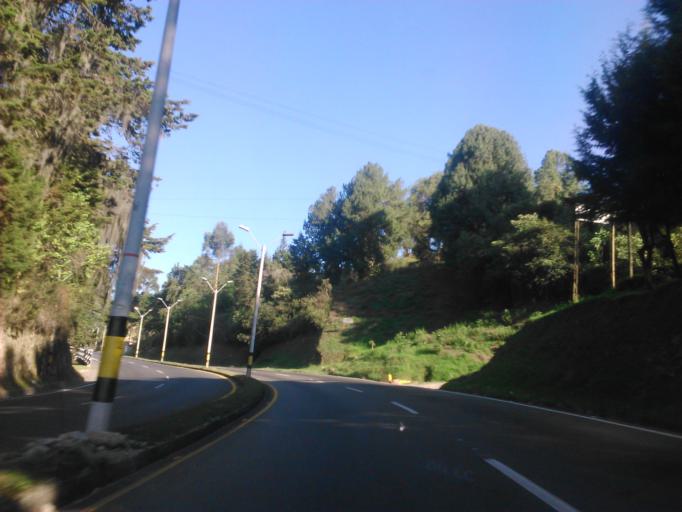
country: CO
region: Antioquia
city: Municipio de Copacabana
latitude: 6.3244
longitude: -75.4705
